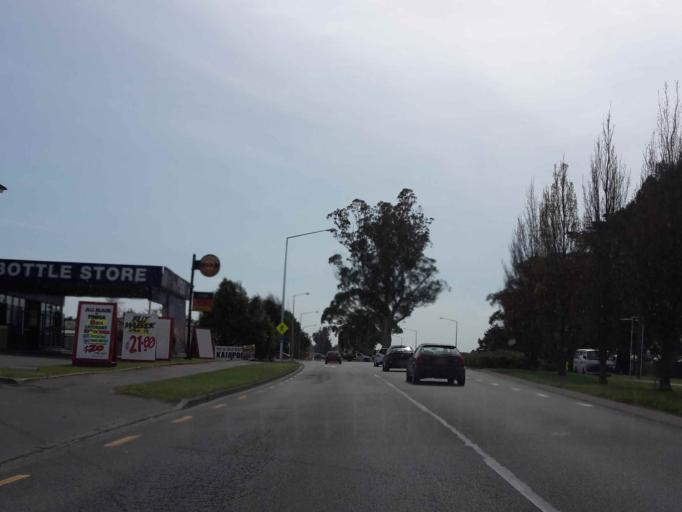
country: NZ
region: Canterbury
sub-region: Waimakariri District
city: Kaiapoi
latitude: -43.4384
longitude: 172.6367
